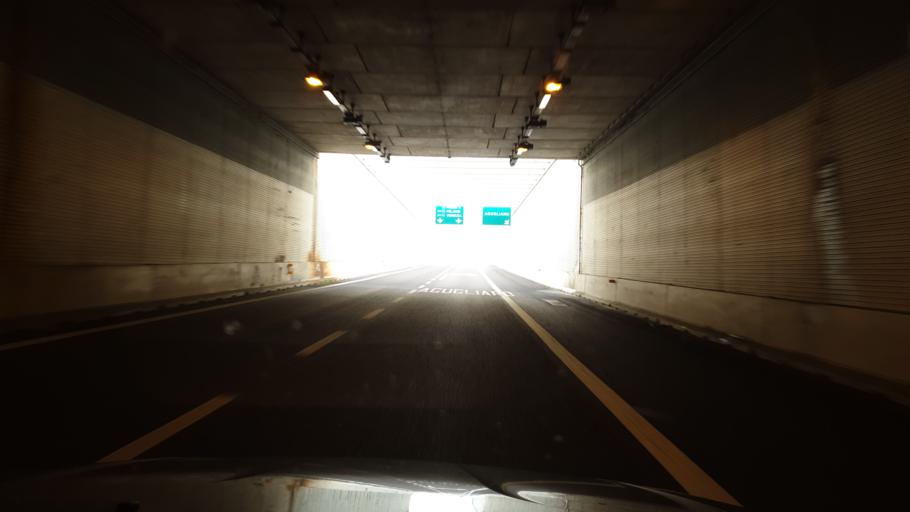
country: IT
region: Veneto
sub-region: Provincia di Vicenza
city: Agugliaro
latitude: 45.3305
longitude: 11.5754
